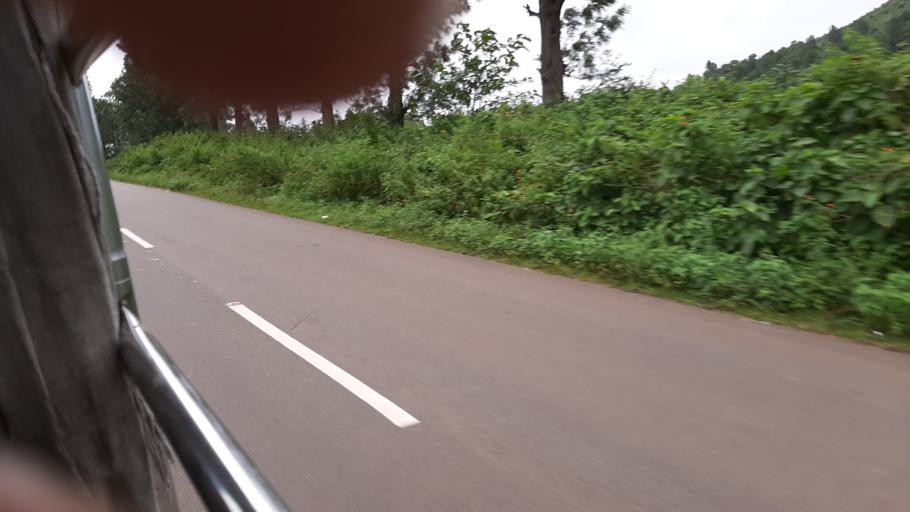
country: IN
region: Andhra Pradesh
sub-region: Vizianagaram District
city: Salur
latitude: 18.2957
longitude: 82.9150
